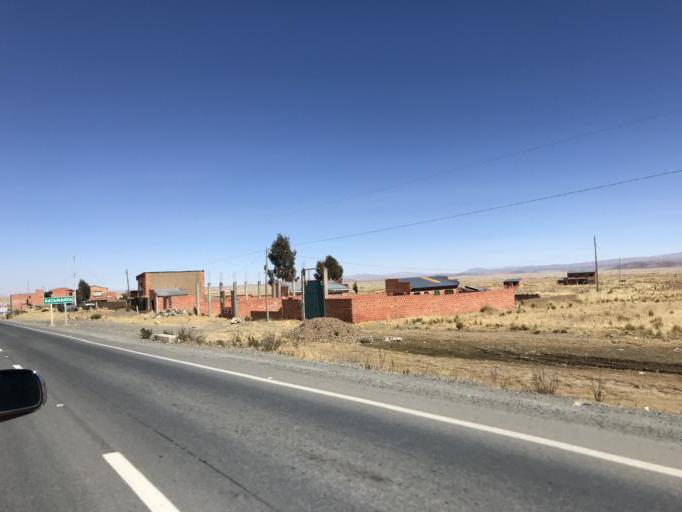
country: BO
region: La Paz
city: Batallas
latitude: -16.3748
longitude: -68.3819
